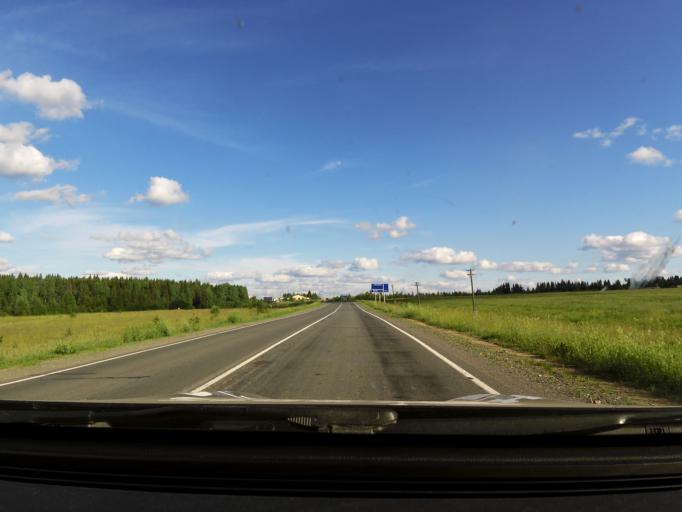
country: RU
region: Kirov
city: Omutninsk
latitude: 58.6877
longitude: 52.1362
